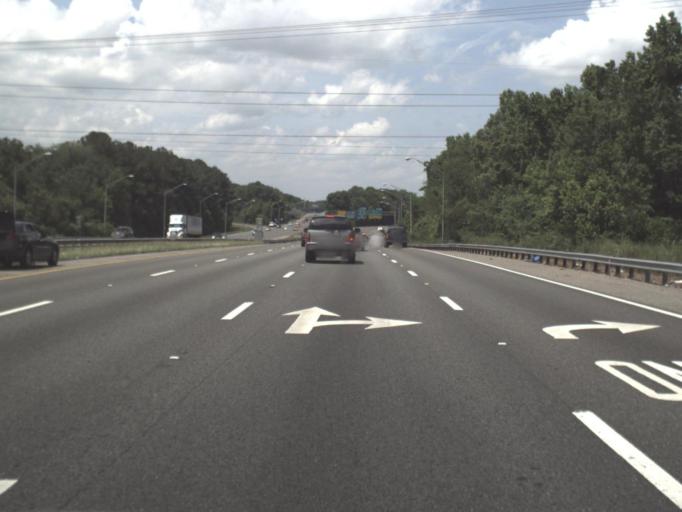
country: US
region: Florida
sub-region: Duval County
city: Jacksonville
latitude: 30.3058
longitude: -81.7701
